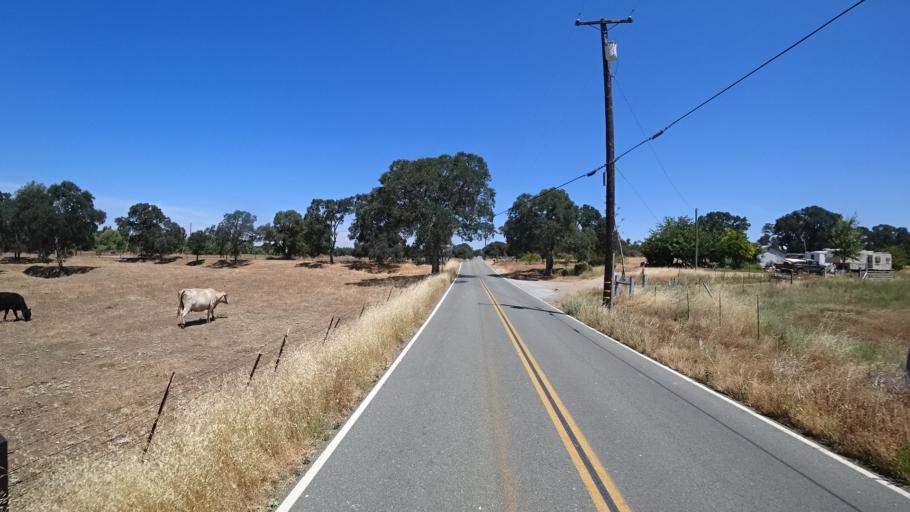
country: US
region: California
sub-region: Calaveras County
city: Rancho Calaveras
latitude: 38.1700
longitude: -120.9183
